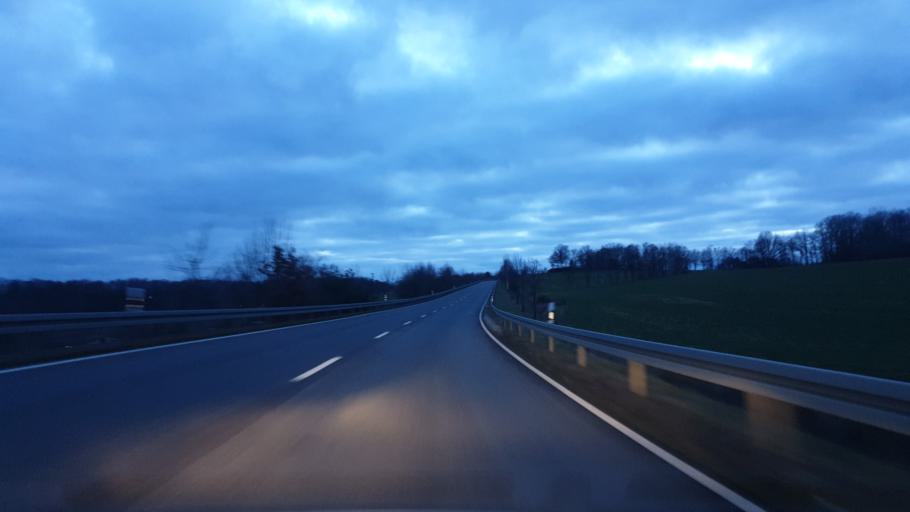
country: DE
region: Saxony
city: Lichtenstein
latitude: 50.7663
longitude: 12.6196
